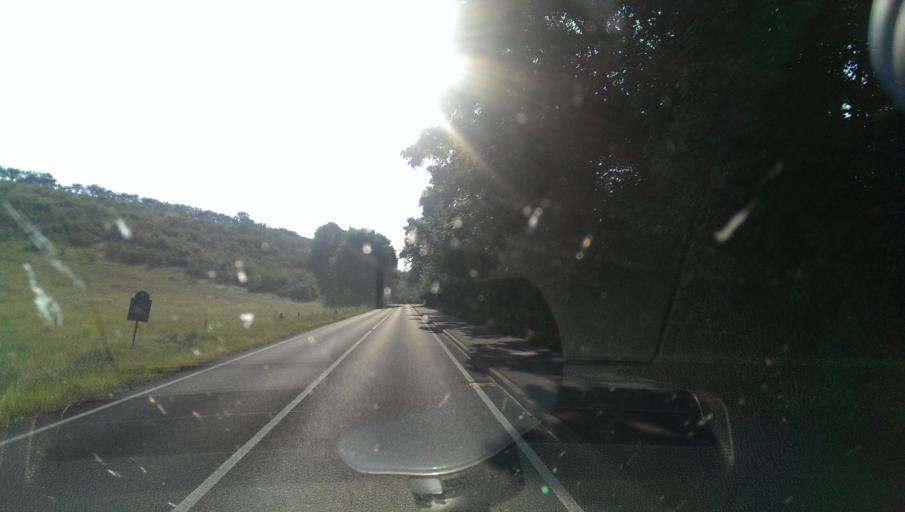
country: DE
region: Thuringia
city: Rohr
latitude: 50.5720
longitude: 10.5156
